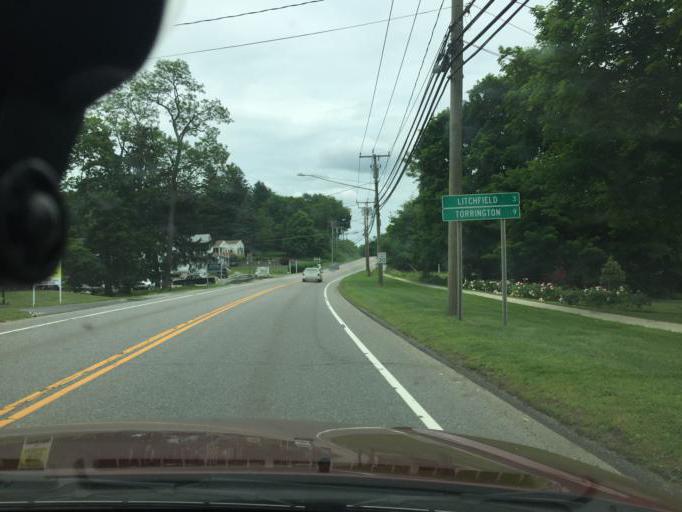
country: US
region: Connecticut
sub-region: Litchfield County
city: Litchfield
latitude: 41.7248
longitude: -73.2354
